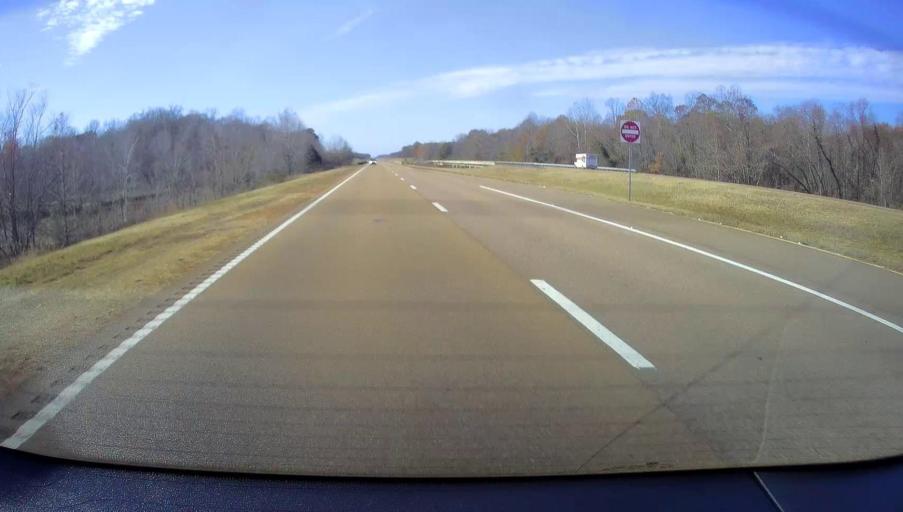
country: US
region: Mississippi
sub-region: Benton County
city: Ashland
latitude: 34.9459
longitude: -89.1936
